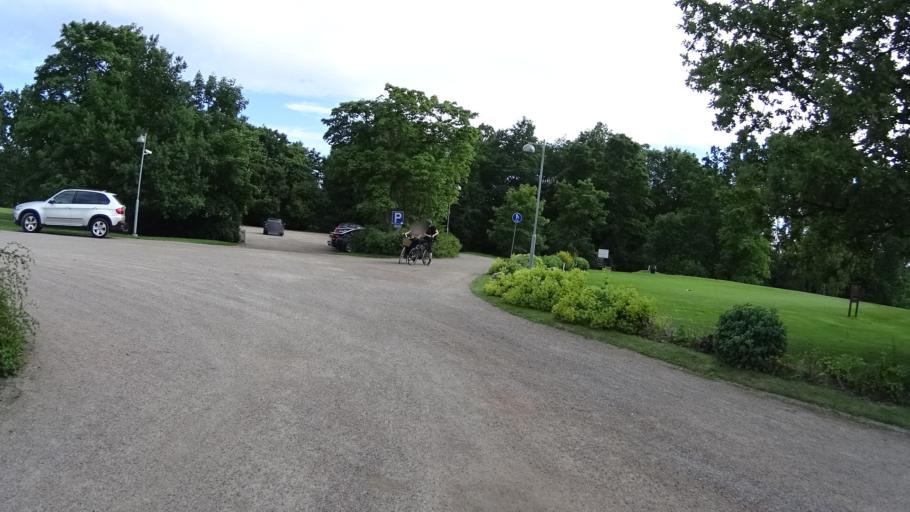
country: FI
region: Uusimaa
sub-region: Helsinki
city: Teekkarikylae
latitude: 60.2118
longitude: 24.8603
